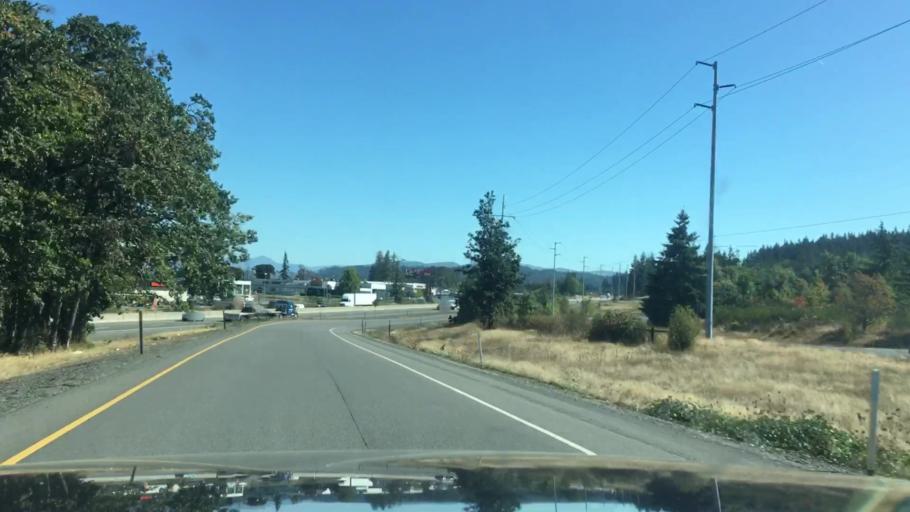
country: US
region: Oregon
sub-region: Lane County
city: Springfield
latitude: 44.0124
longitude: -123.0239
